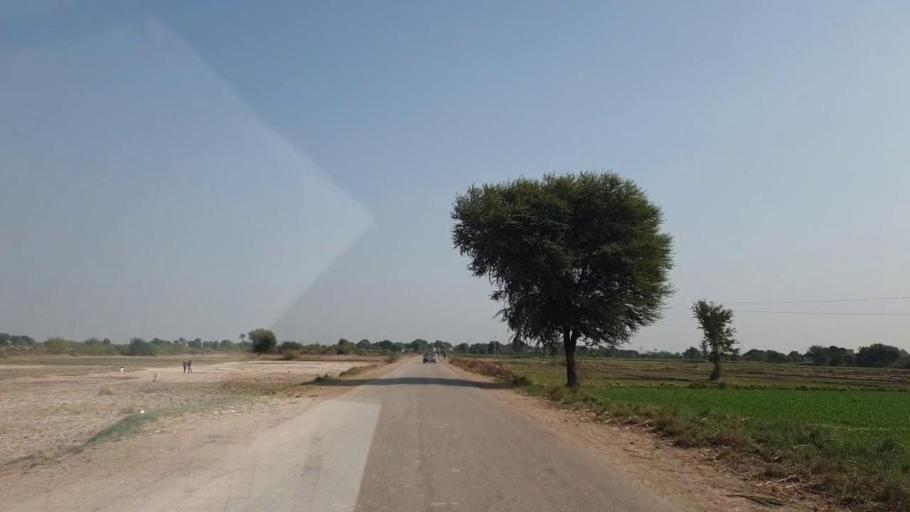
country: PK
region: Sindh
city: Matiari
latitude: 25.5021
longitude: 68.4386
